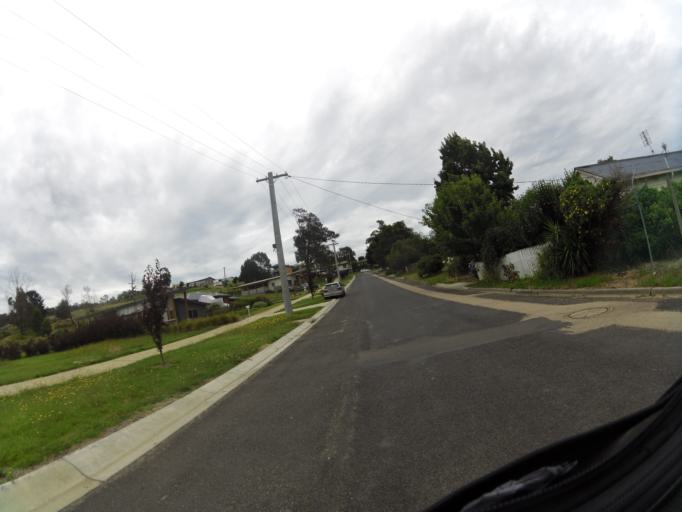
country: AU
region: Victoria
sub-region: East Gippsland
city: Lakes Entrance
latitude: -37.7049
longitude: 147.8220
